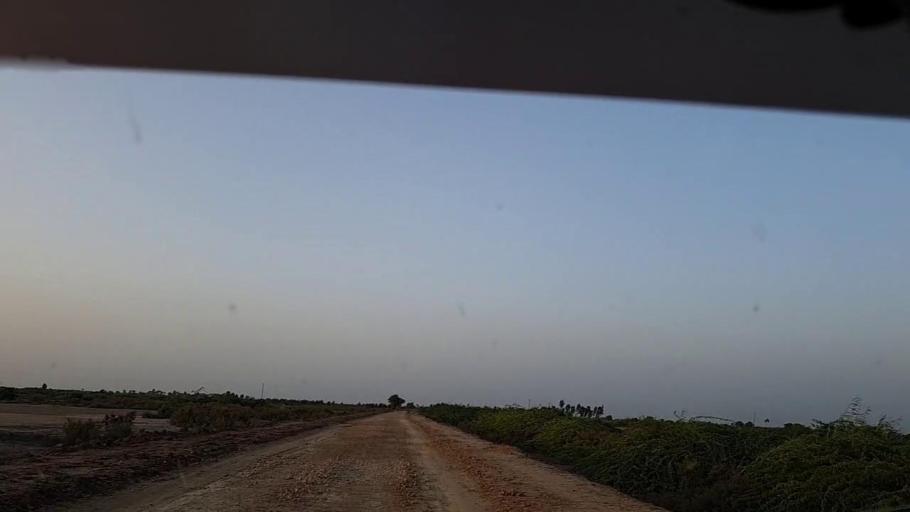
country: PK
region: Sindh
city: Kadhan
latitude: 24.5265
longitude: 68.9436
